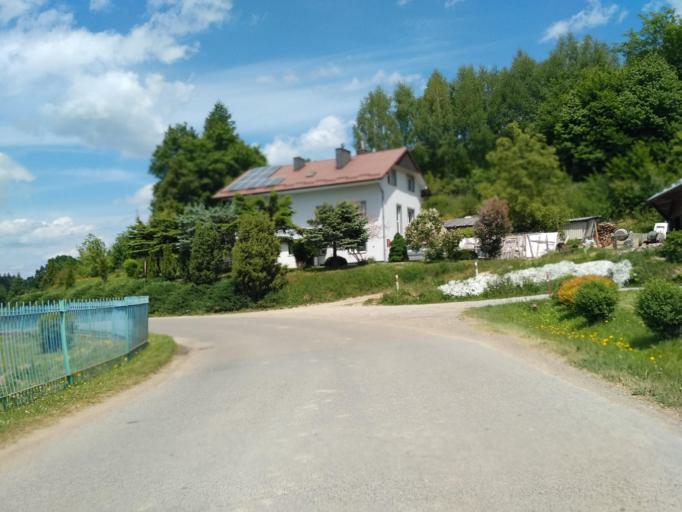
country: PL
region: Subcarpathian Voivodeship
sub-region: Powiat krosnienski
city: Dukla
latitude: 49.5845
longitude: 21.6239
